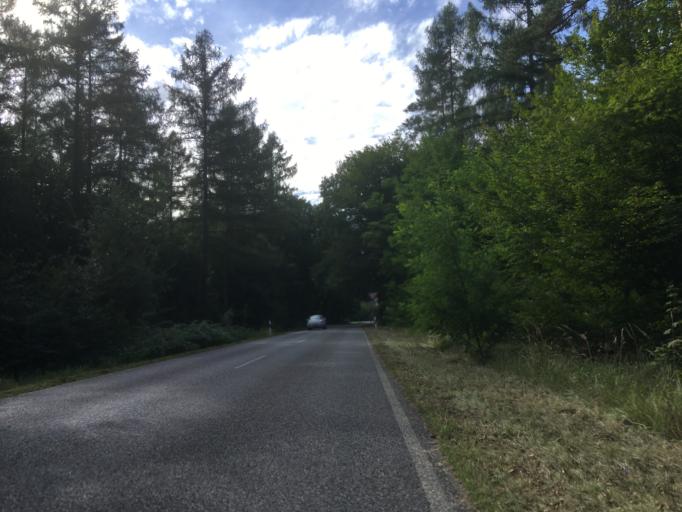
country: DE
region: Brandenburg
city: Chorin
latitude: 52.9179
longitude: 13.9061
